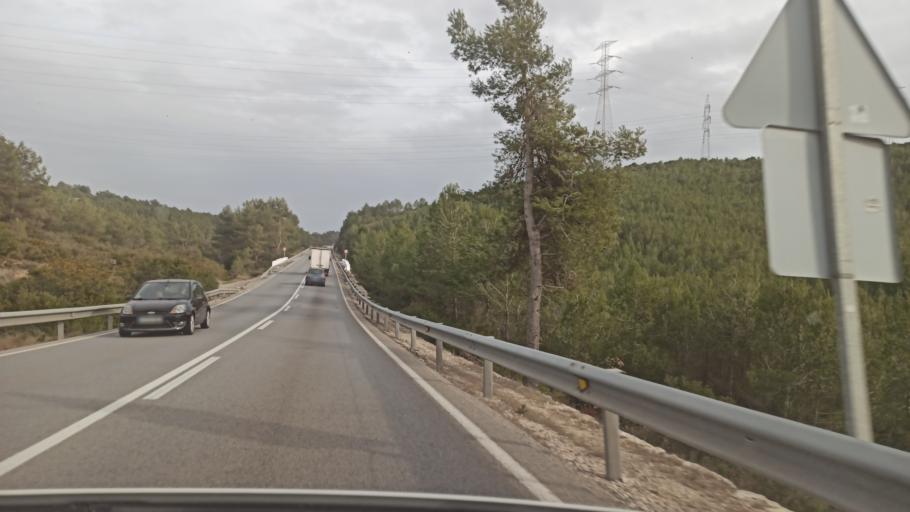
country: ES
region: Catalonia
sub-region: Provincia de Barcelona
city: Subirats
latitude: 41.3929
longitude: 1.8625
